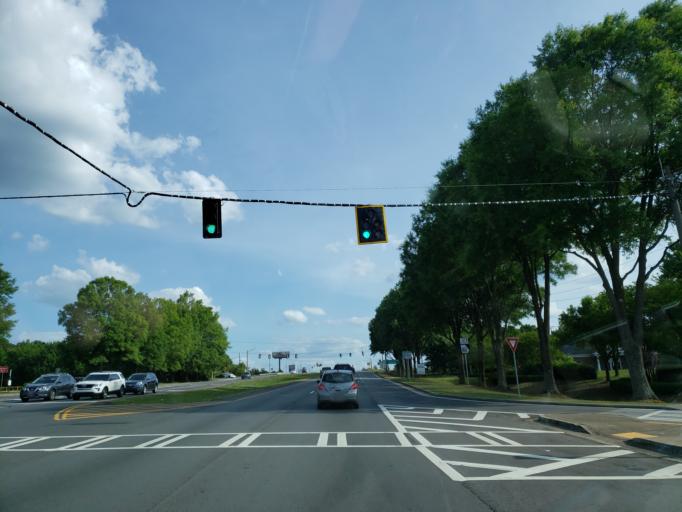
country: US
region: Georgia
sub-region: Carroll County
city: Carrollton
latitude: 33.5605
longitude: -85.0732
